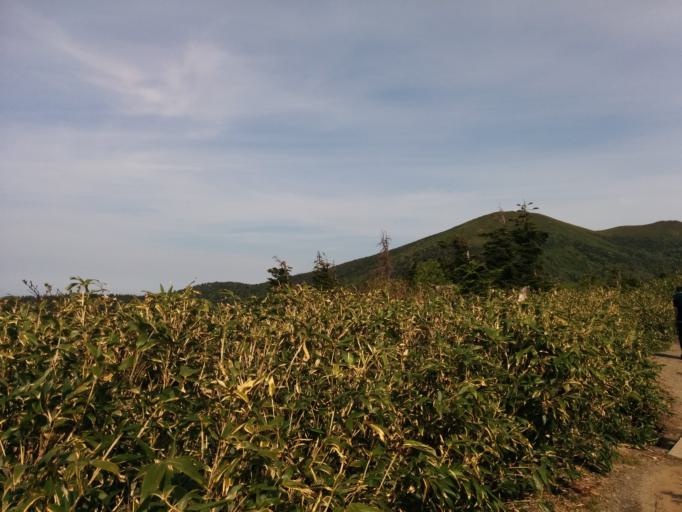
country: JP
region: Aomori
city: Aomori Shi
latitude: 40.6759
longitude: 140.8613
